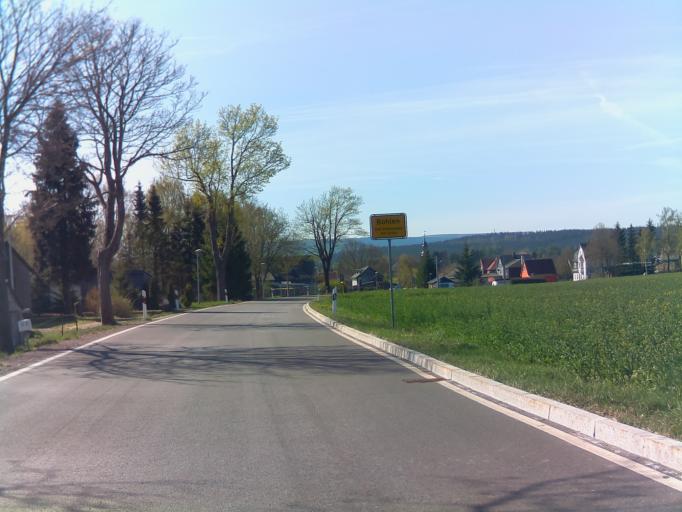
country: DE
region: Thuringia
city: Bohlen
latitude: 50.5931
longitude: 11.0427
